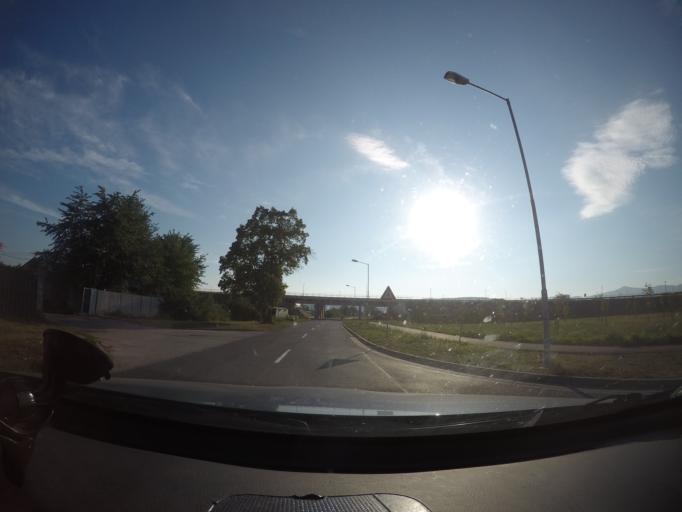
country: SK
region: Trenciansky
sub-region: Okres Trencin
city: Trencin
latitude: 48.8797
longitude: 18.0131
